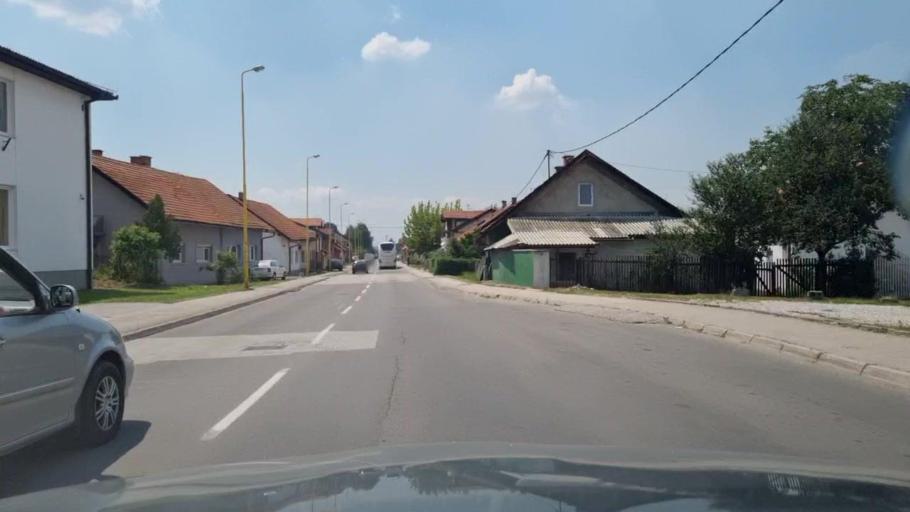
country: BA
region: Federation of Bosnia and Herzegovina
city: Tuzla
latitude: 44.5312
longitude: 18.6500
